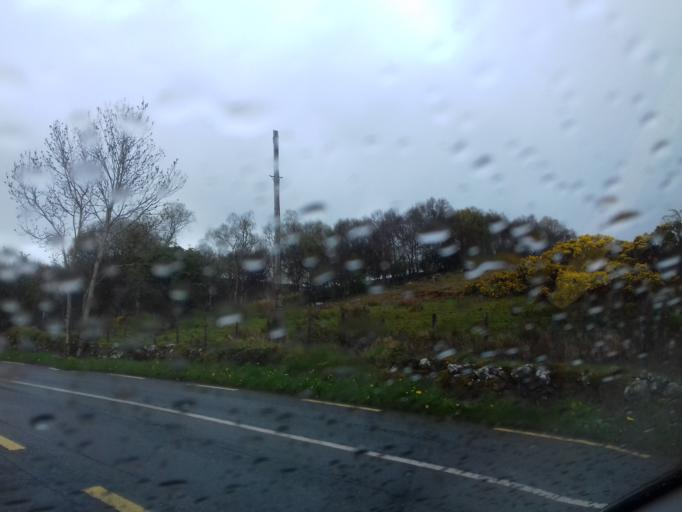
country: IE
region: Connaught
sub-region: County Leitrim
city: Manorhamilton
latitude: 54.2630
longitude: -7.9423
